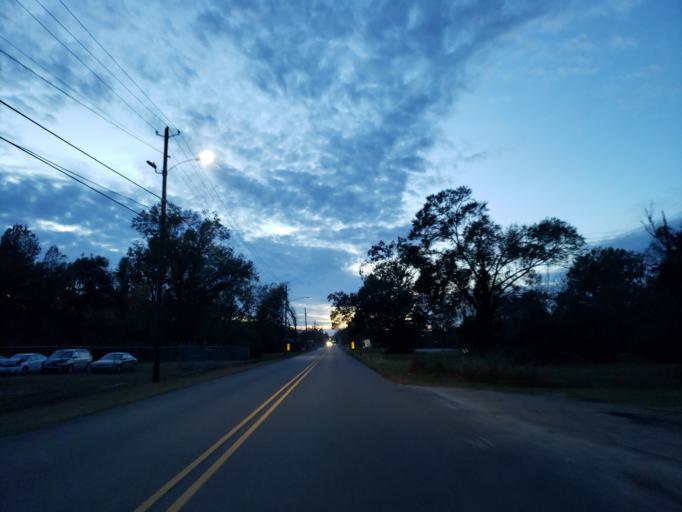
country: US
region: Mississippi
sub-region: Forrest County
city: Hattiesburg
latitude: 31.3251
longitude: -89.2723
